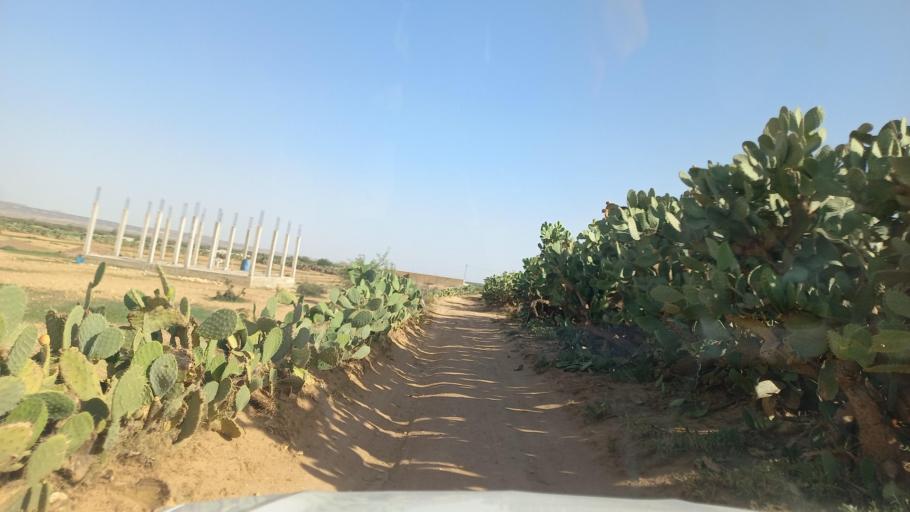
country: TN
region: Al Qasrayn
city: Sbiba
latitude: 35.3221
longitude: 9.0237
